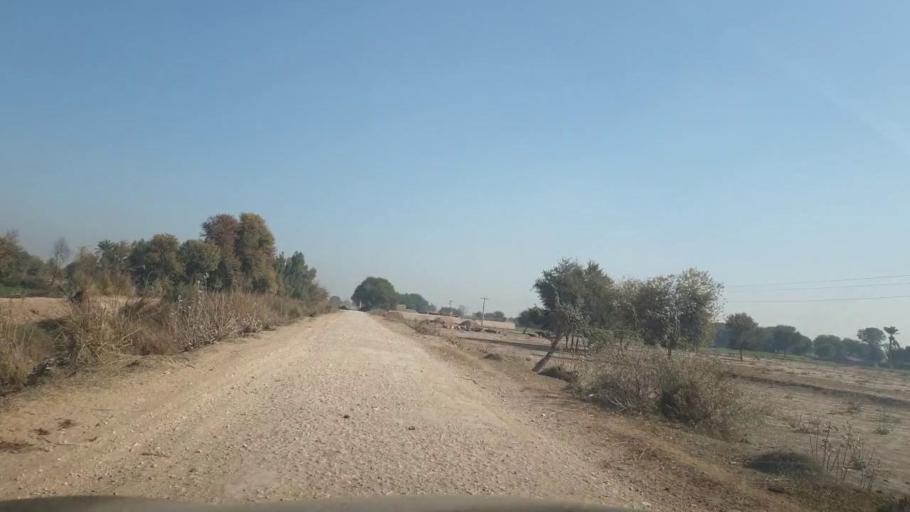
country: PK
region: Sindh
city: Mirpur Mathelo
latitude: 28.1295
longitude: 69.5008
